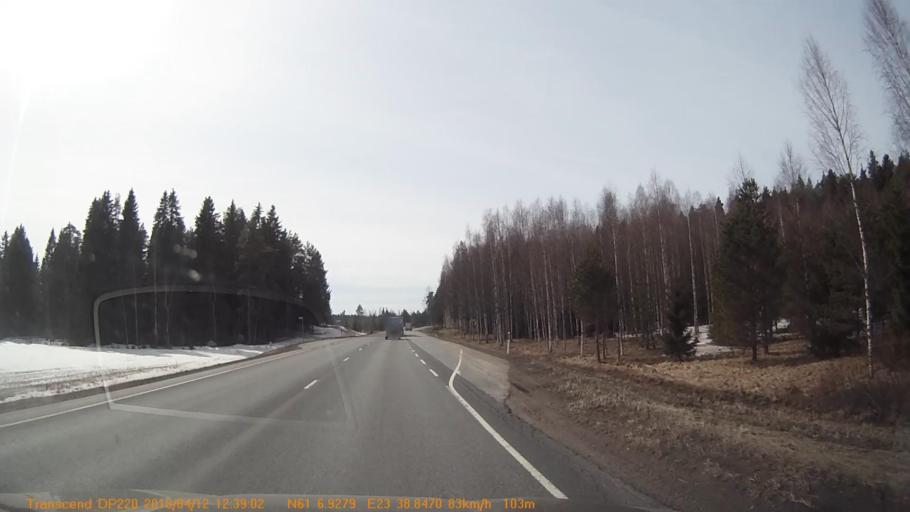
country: FI
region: Pirkanmaa
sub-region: Etelae-Pirkanmaa
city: Kylmaekoski
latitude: 61.1155
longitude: 23.6476
